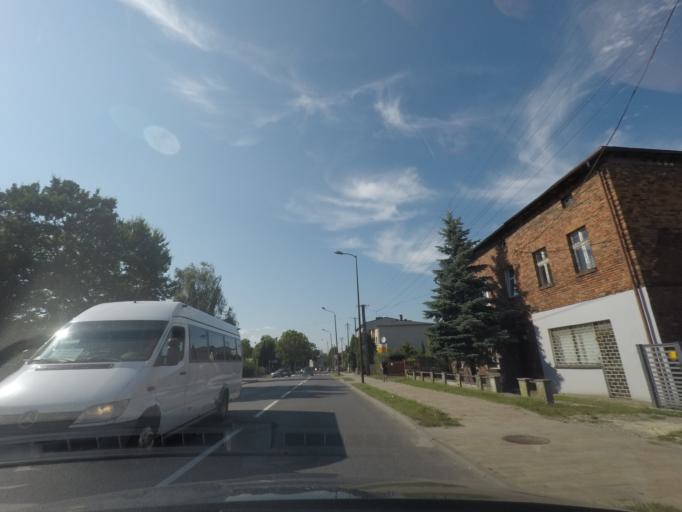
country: PL
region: Silesian Voivodeship
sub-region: Zory
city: Zory
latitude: 50.0489
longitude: 18.6904
